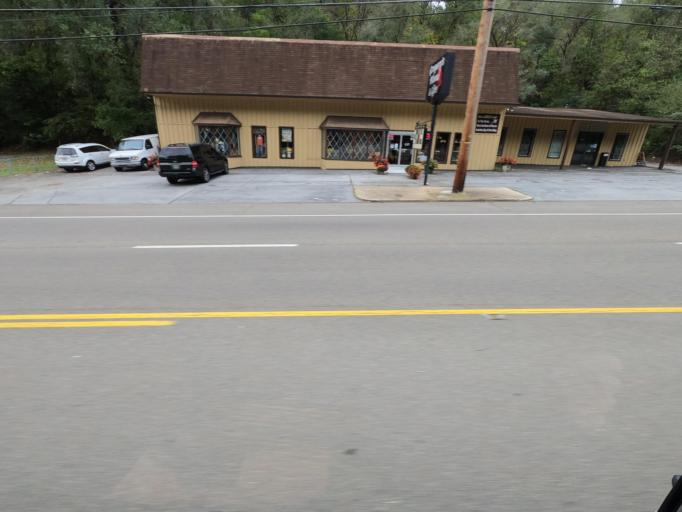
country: US
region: Tennessee
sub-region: Sullivan County
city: Kingsport
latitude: 36.5678
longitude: -82.5652
